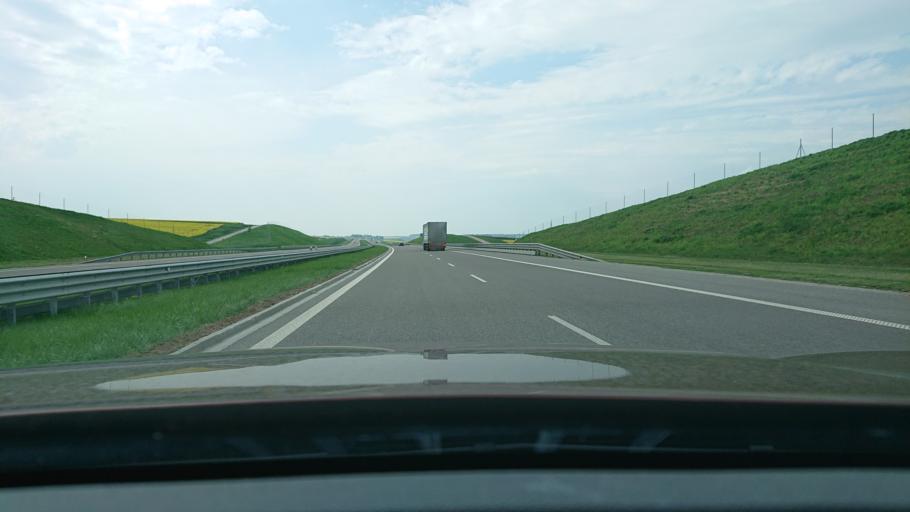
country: PL
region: Subcarpathian Voivodeship
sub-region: Powiat jaroslawski
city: Rokietnica
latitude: 49.9316
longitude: 22.7117
